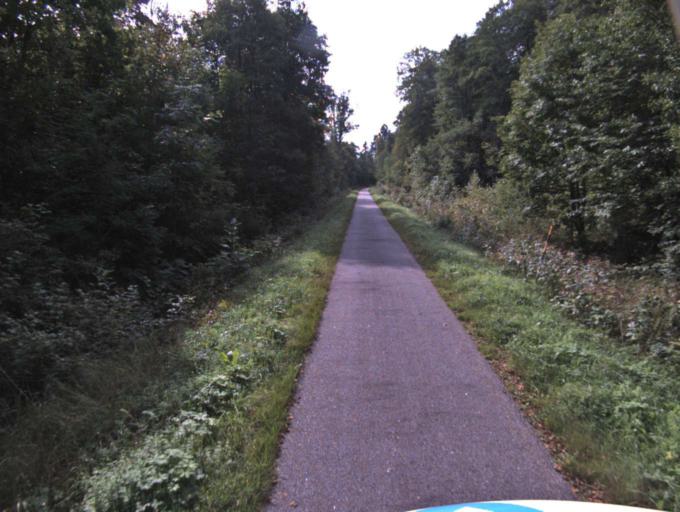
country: SE
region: Vaestra Goetaland
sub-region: Tranemo Kommun
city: Limmared
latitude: 57.6592
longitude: 13.3626
